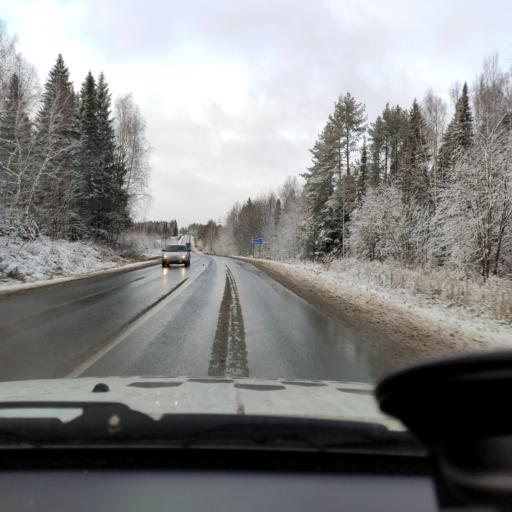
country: RU
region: Perm
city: Nytva
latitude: 57.9318
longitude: 55.3877
